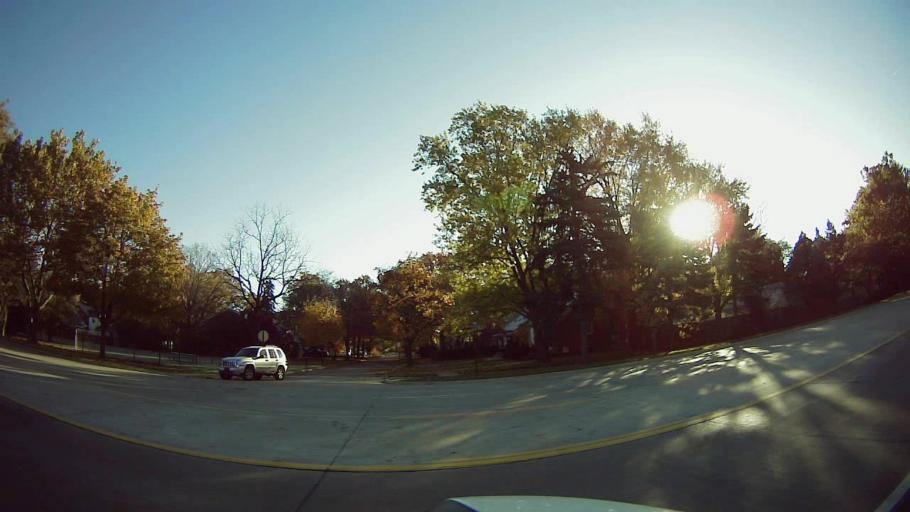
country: US
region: Michigan
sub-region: Oakland County
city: Huntington Woods
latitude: 42.4770
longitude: -83.1828
